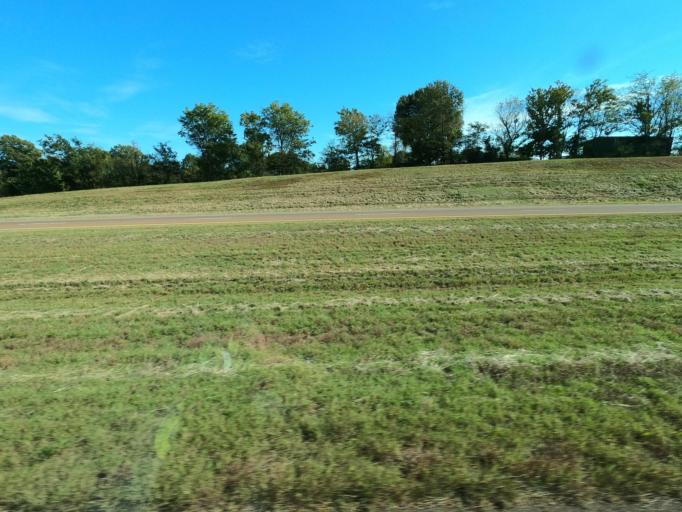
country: US
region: Tennessee
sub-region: Dyer County
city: Newbern
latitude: 36.1282
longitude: -89.2748
